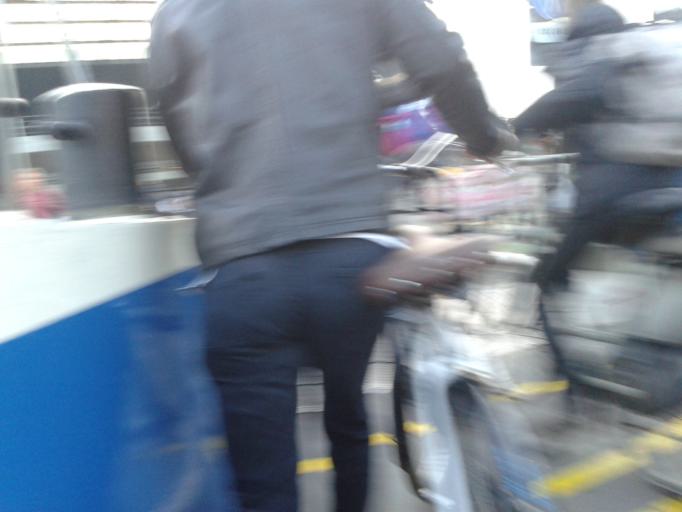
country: NL
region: North Holland
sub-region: Gemeente Amsterdam
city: Amsterdam
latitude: 52.3807
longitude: 4.8996
